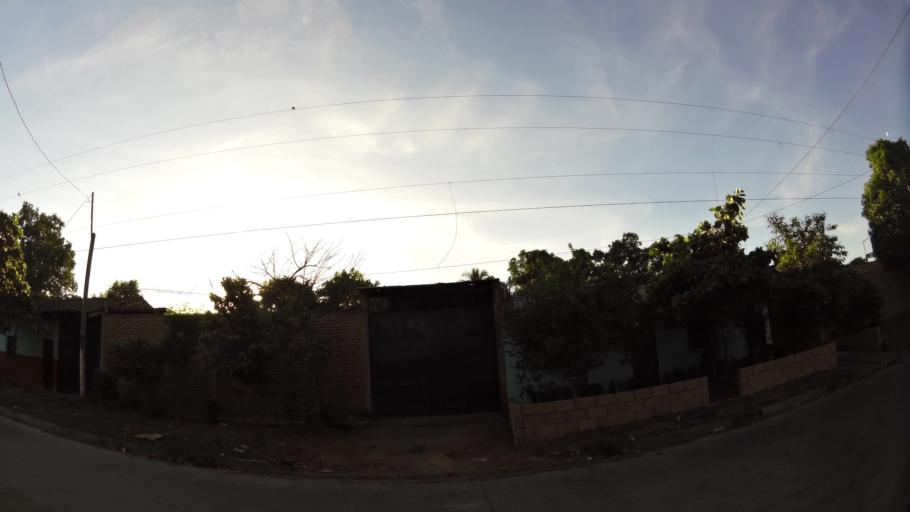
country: SV
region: San Miguel
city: San Miguel
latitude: 13.4623
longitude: -88.1763
